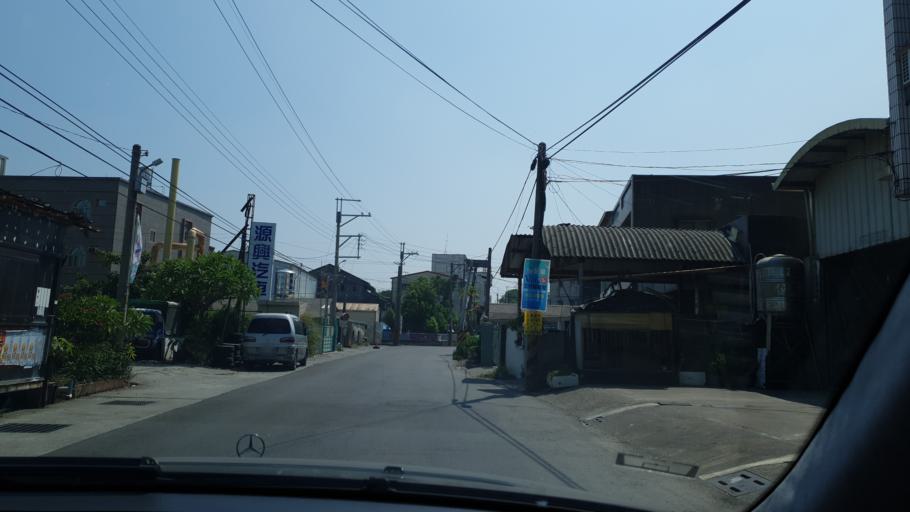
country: TW
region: Taiwan
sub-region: Yunlin
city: Douliu
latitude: 23.7481
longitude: 120.4221
